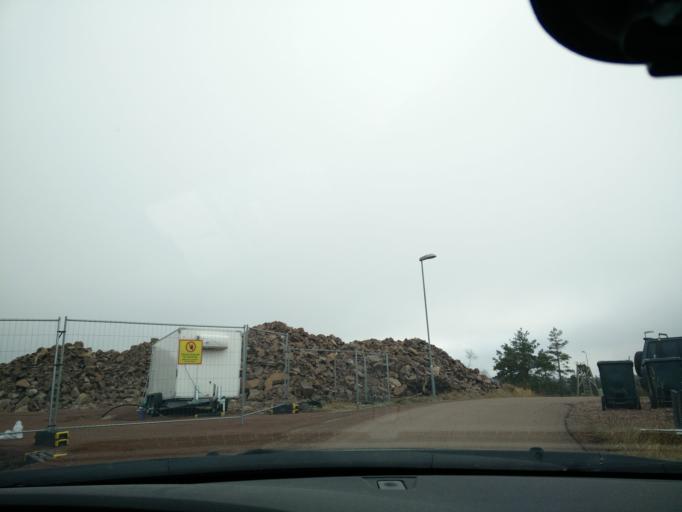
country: AX
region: Alands landsbygd
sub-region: Jomala
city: Jomala
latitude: 60.1306
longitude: 19.9277
